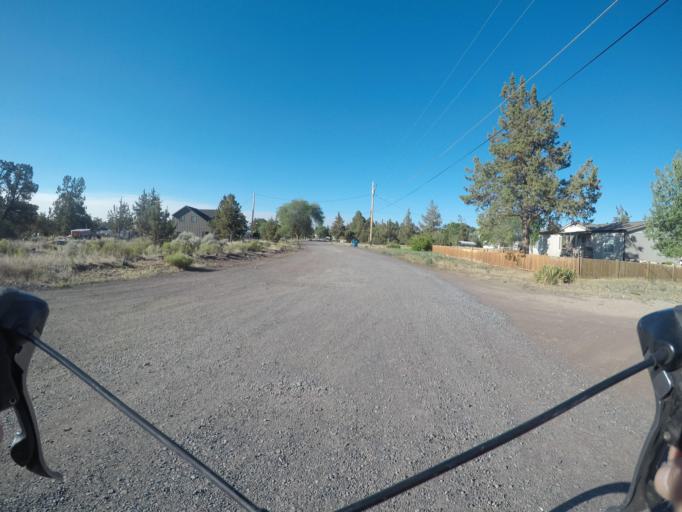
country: US
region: Oregon
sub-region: Deschutes County
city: Redmond
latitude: 44.2215
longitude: -121.2360
